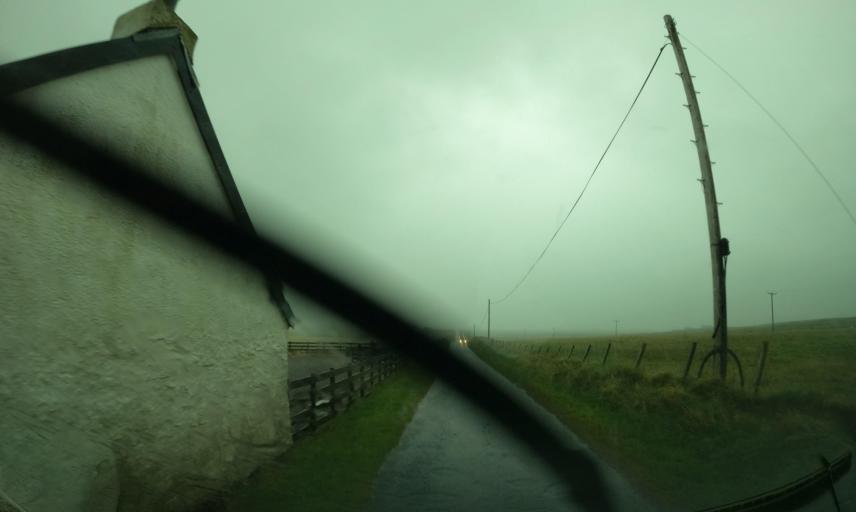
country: GB
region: Scotland
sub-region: Eilean Siar
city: Barra
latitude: 56.4621
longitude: -6.9300
